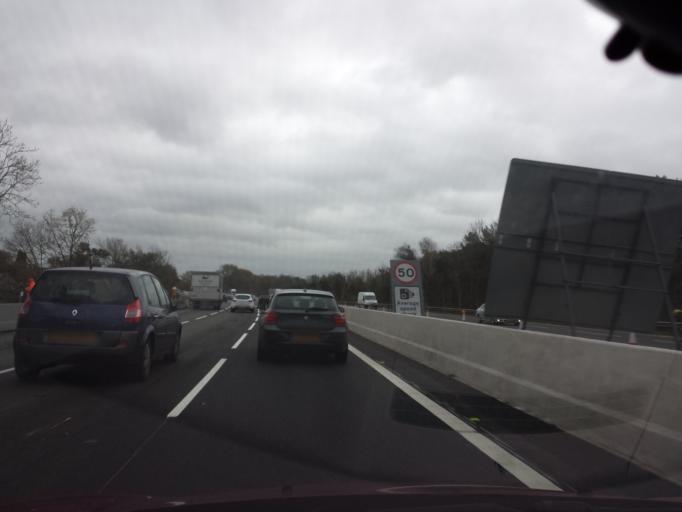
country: GB
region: England
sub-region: Surrey
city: Windlesham
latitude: 51.3586
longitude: -0.6609
